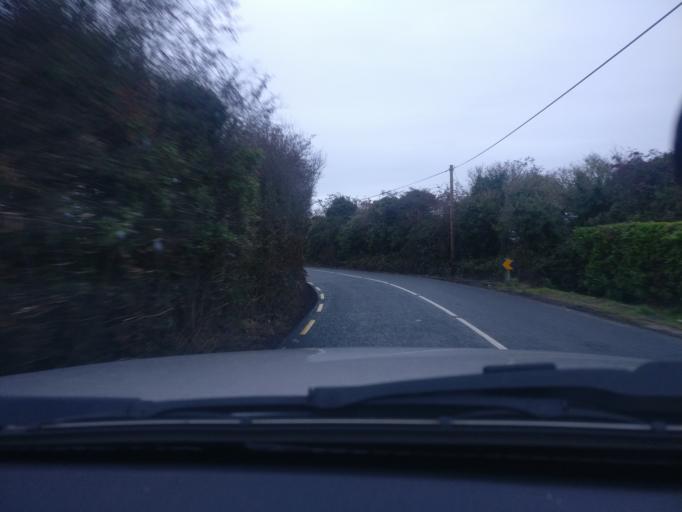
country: IE
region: Leinster
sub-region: Kildare
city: Kilcock
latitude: 53.4536
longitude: -6.6248
